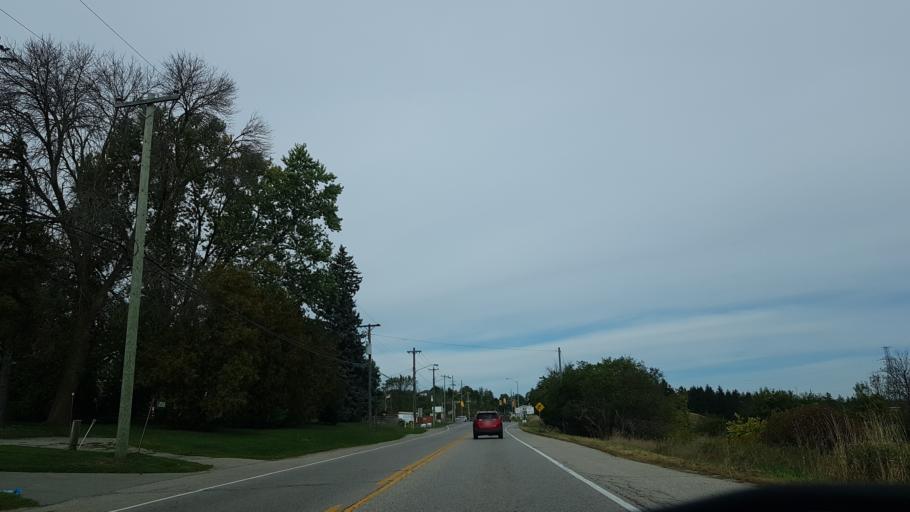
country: CA
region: Ontario
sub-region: Wellington County
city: Guelph
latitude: 43.5171
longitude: -80.2681
